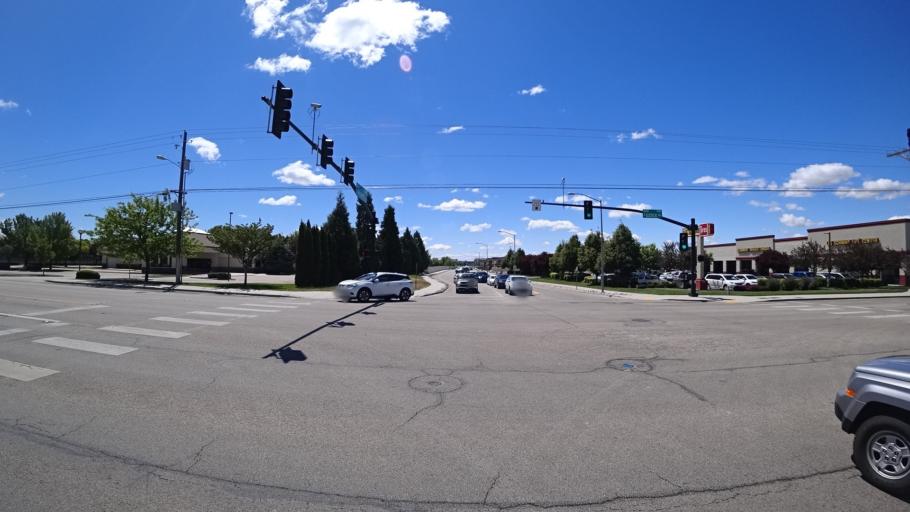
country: US
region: Idaho
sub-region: Ada County
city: Meridian
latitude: 43.6339
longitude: -116.3496
